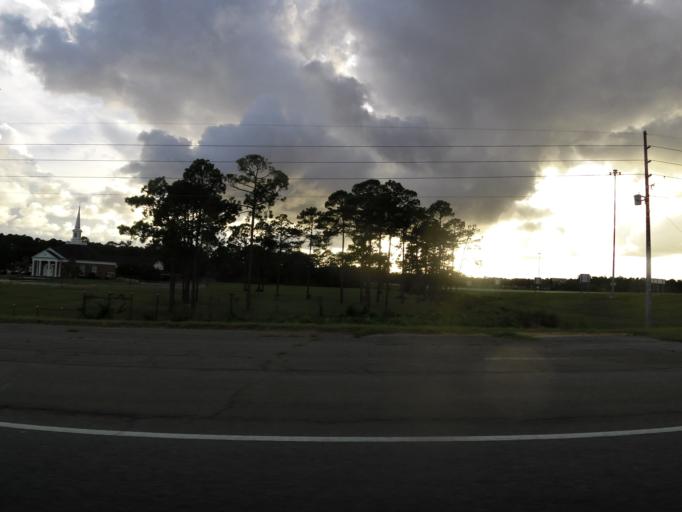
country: US
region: Georgia
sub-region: Glynn County
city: Dock Junction
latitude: 31.2391
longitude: -81.5021
